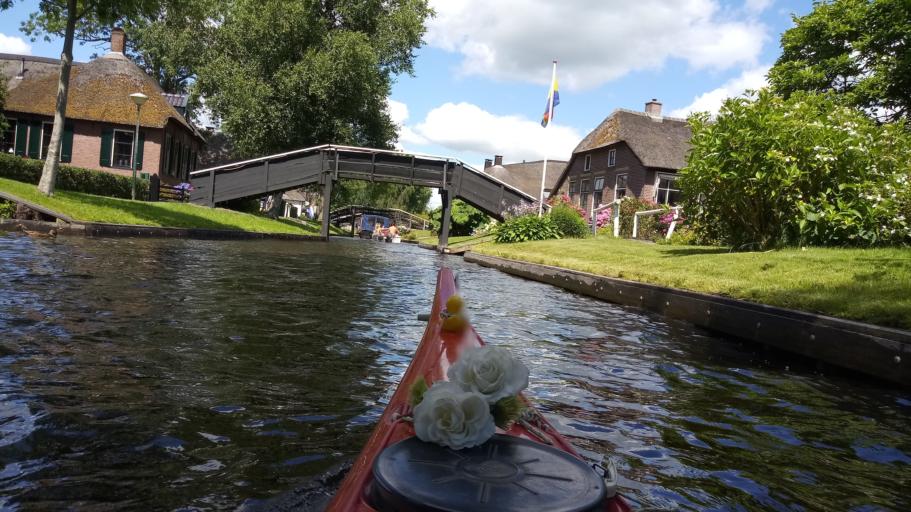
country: NL
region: Overijssel
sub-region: Gemeente Steenwijkerland
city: Giethoorn
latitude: 52.7126
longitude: 6.0816
